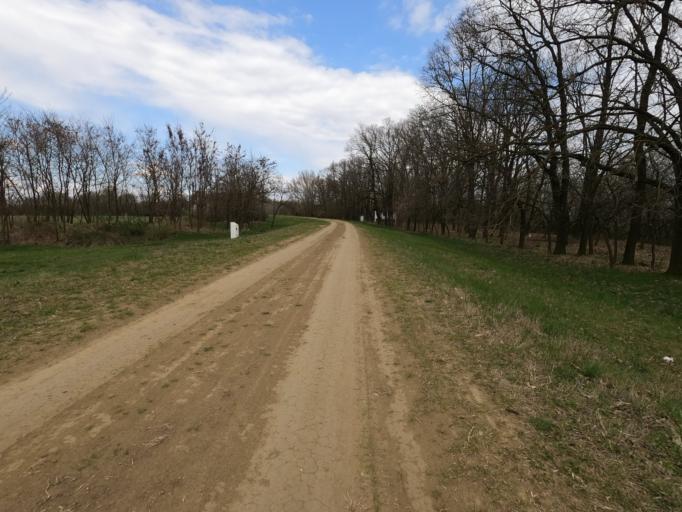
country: HU
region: Jasz-Nagykun-Szolnok
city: Turkeve
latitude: 47.0852
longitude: 20.7650
